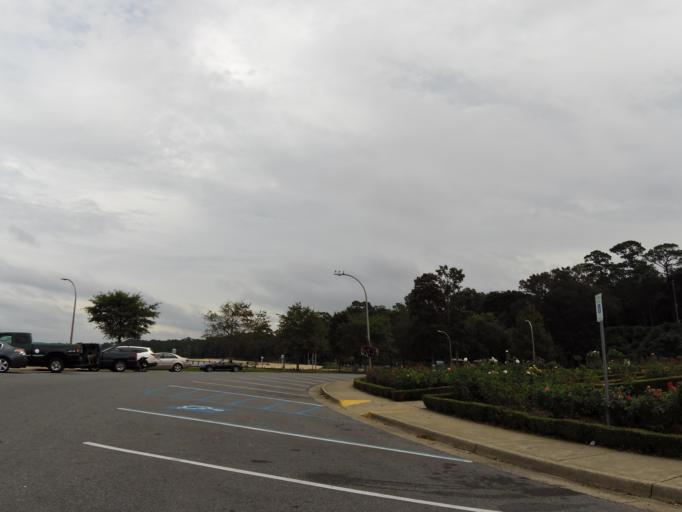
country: US
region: Alabama
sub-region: Baldwin County
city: Fairhope
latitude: 30.5243
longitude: -87.9125
